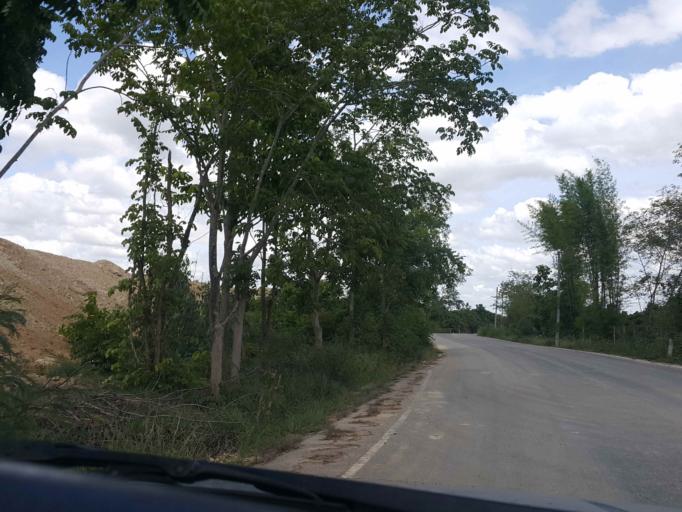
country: TH
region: Chiang Mai
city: Doi Lo
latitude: 18.4785
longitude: 98.7472
